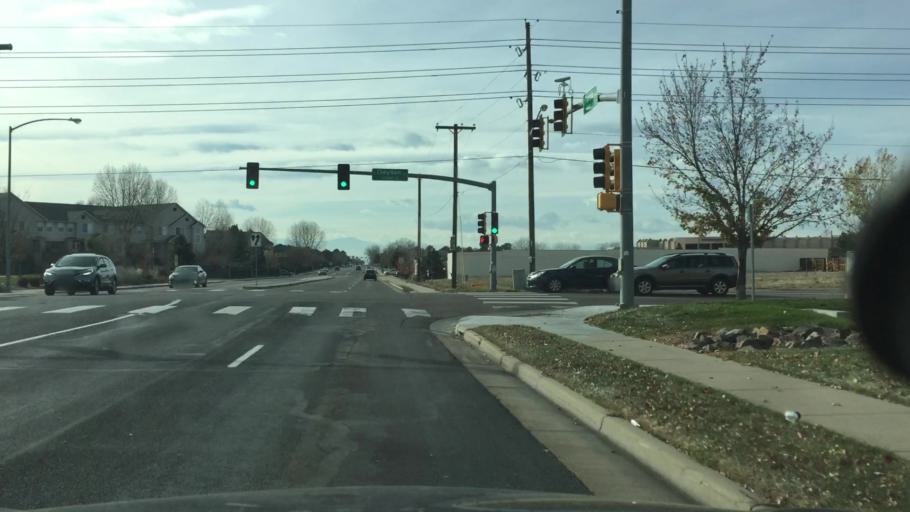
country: US
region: Colorado
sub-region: Adams County
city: Aurora
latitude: 39.6894
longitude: -104.8750
